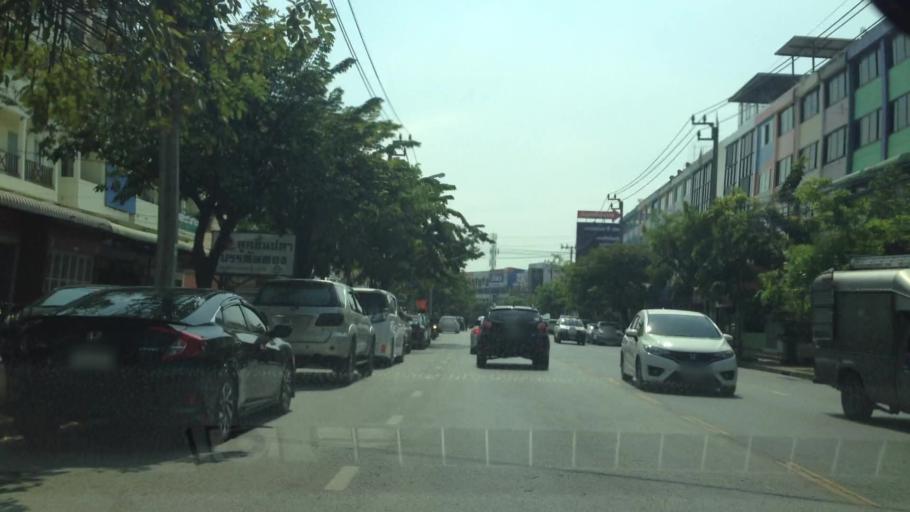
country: TH
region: Bangkok
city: Bang Khen
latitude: 13.8972
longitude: 100.6381
